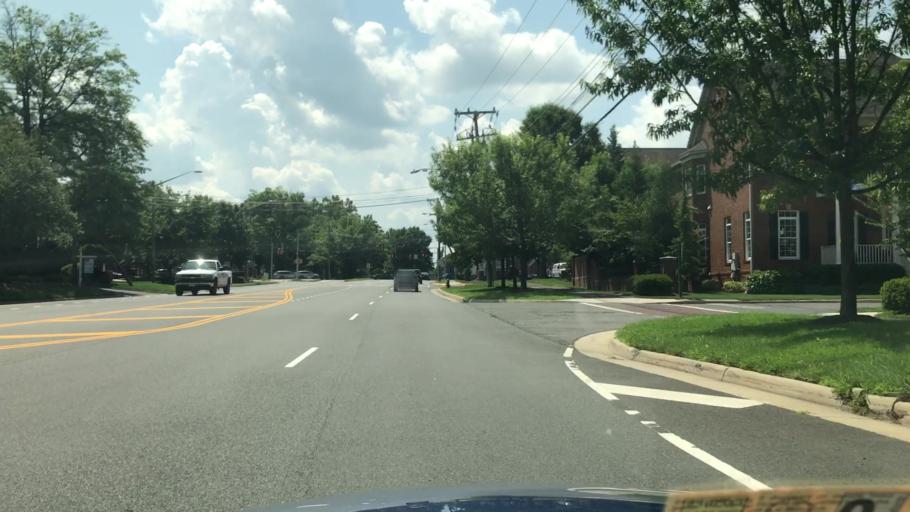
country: US
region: Virginia
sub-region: Fairfax County
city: Oakton
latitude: 38.8826
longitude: -77.3012
